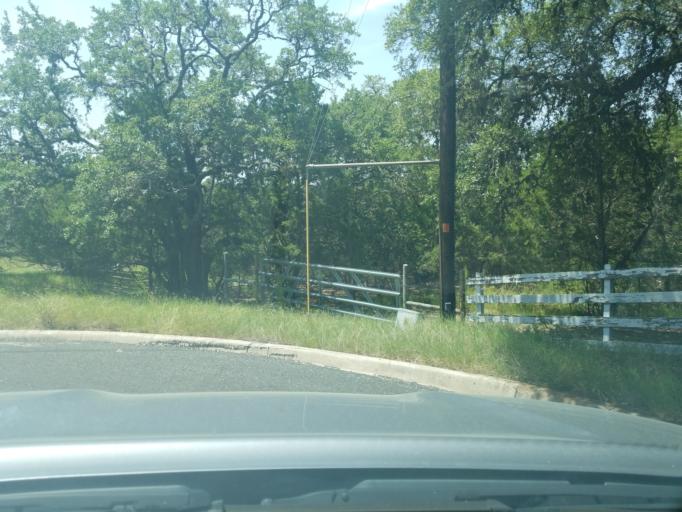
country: US
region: Texas
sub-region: Bexar County
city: Timberwood Park
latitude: 29.6730
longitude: -98.5044
